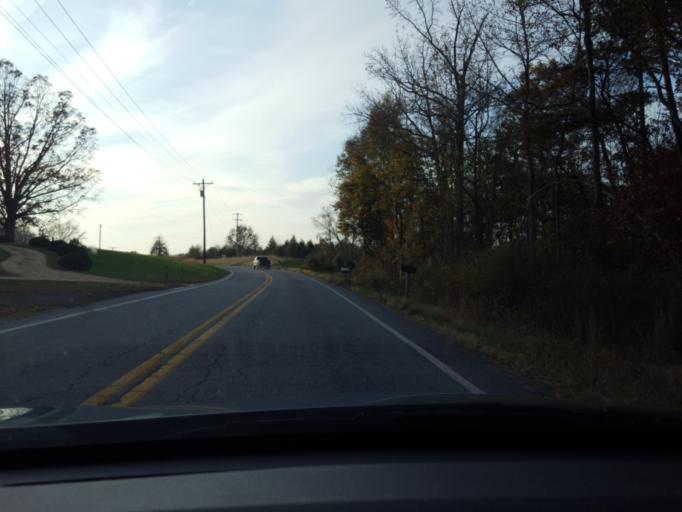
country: US
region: Maryland
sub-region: Charles County
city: Hughesville
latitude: 38.5252
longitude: -76.8253
